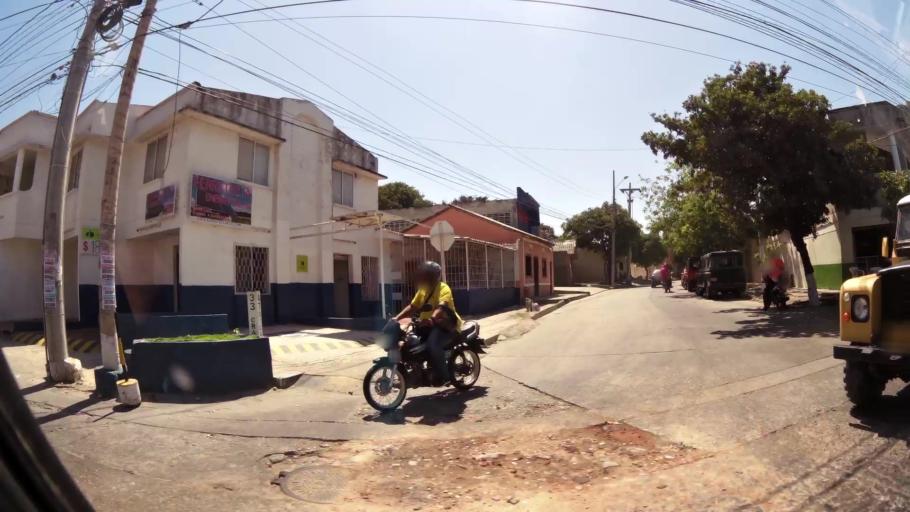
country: CO
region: Atlantico
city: Barranquilla
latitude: 10.9755
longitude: -74.7898
